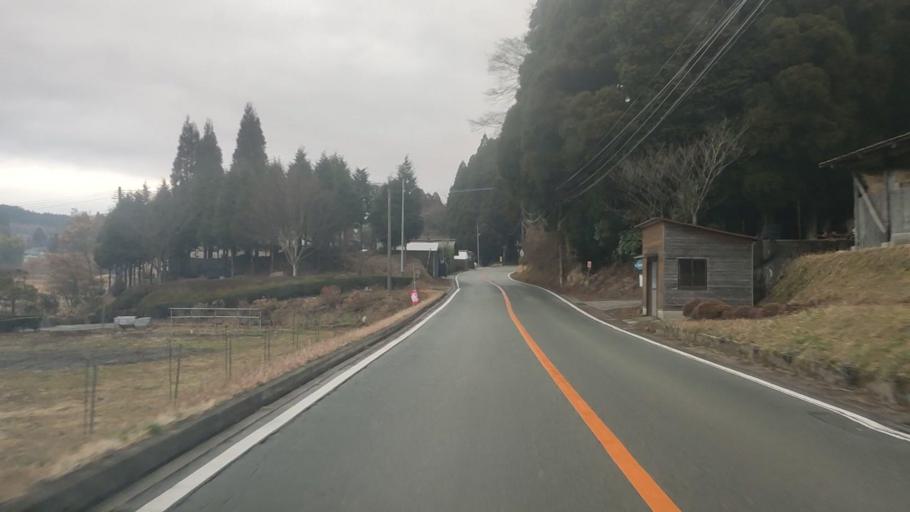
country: JP
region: Kumamoto
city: Aso
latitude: 32.8547
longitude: 131.1549
